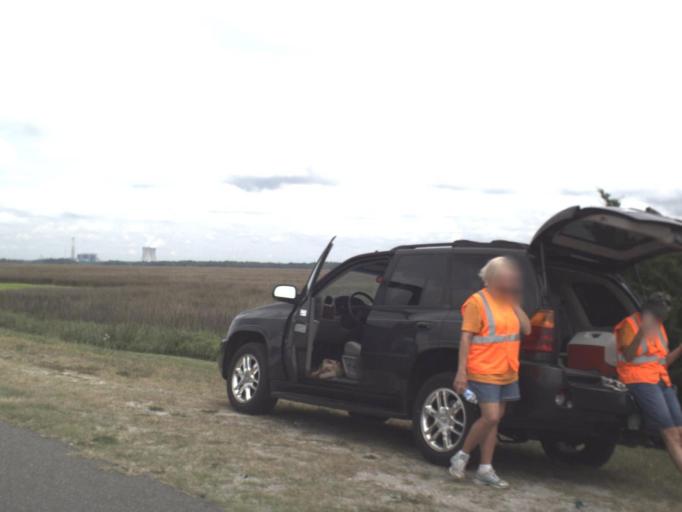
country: US
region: Florida
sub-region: Duval County
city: Atlantic Beach
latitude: 30.4003
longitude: -81.4795
